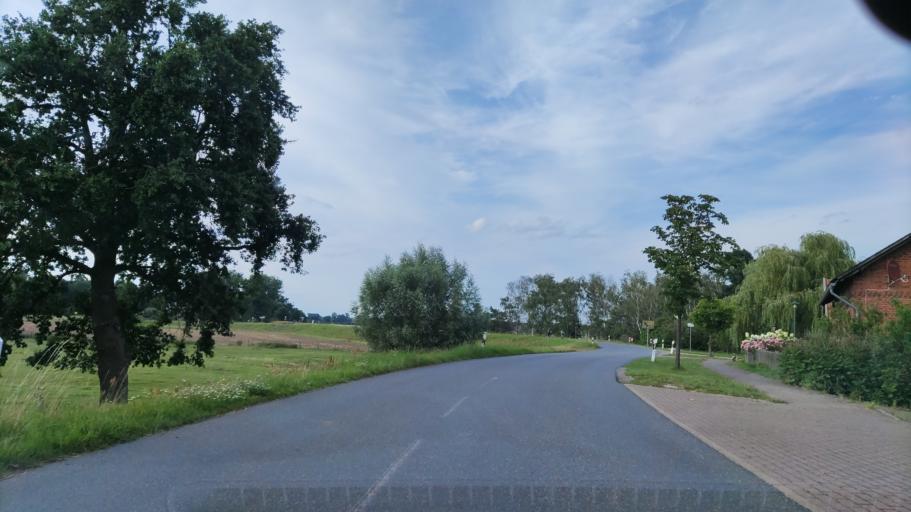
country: DE
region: Lower Saxony
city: Dannenberg
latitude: 53.1381
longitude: 11.1223
